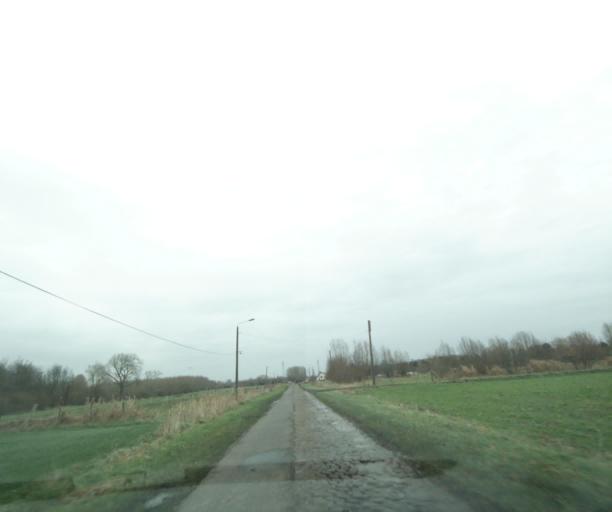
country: FR
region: Nord-Pas-de-Calais
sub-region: Departement du Nord
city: Fresnes-sur-Escaut
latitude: 50.4224
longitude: 3.5909
